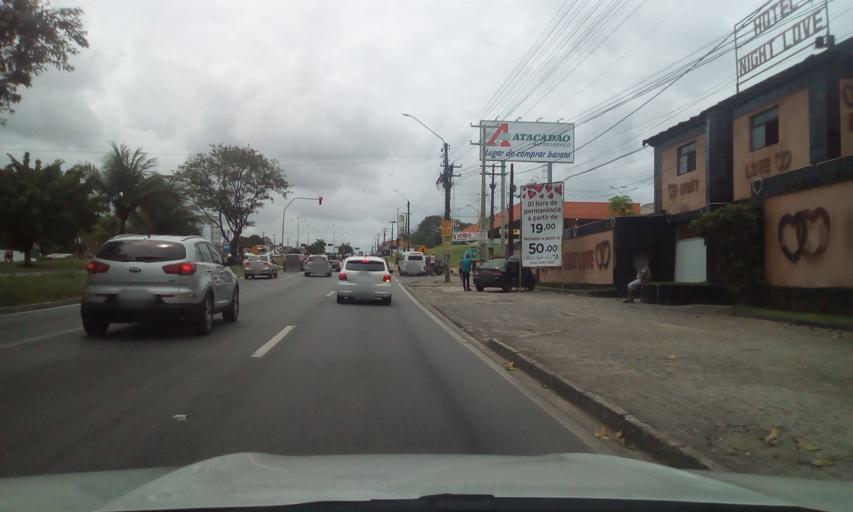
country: BR
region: Pernambuco
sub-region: Abreu E Lima
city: Abreu e Lima
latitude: -7.8812
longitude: -34.9049
